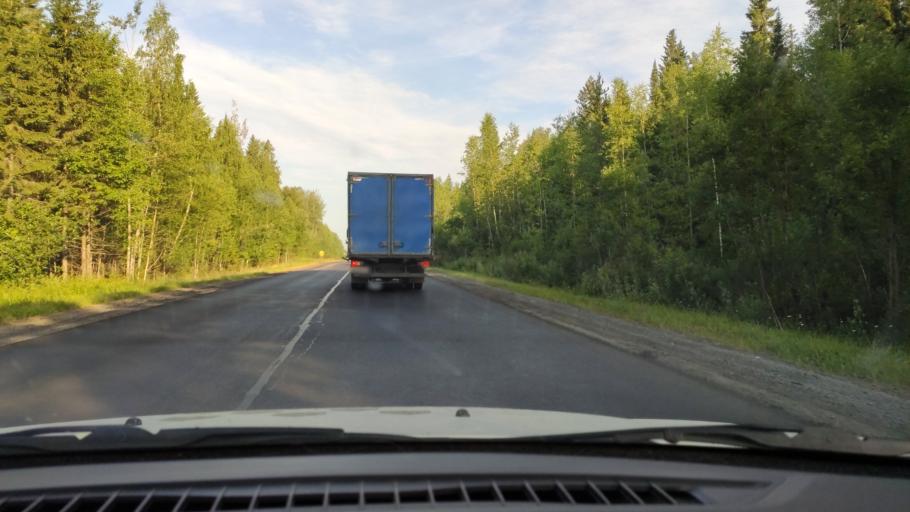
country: RU
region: Kirov
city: Omutninsk
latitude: 58.7605
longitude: 52.0115
